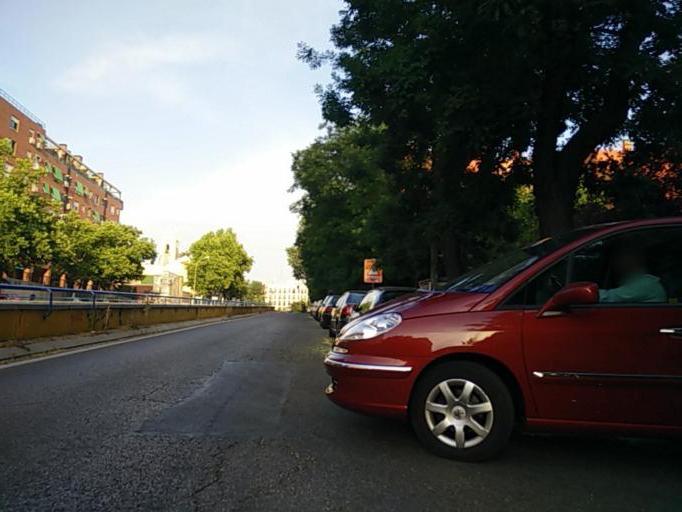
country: ES
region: Madrid
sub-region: Provincia de Madrid
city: Madrid
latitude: 40.4074
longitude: -3.7140
